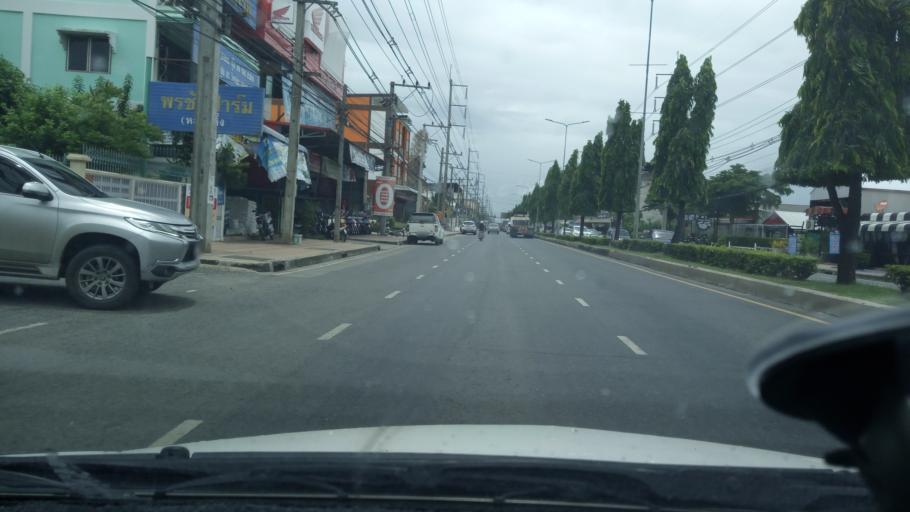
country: TH
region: Chon Buri
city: Phanat Nikhom
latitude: 13.4548
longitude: 101.1747
